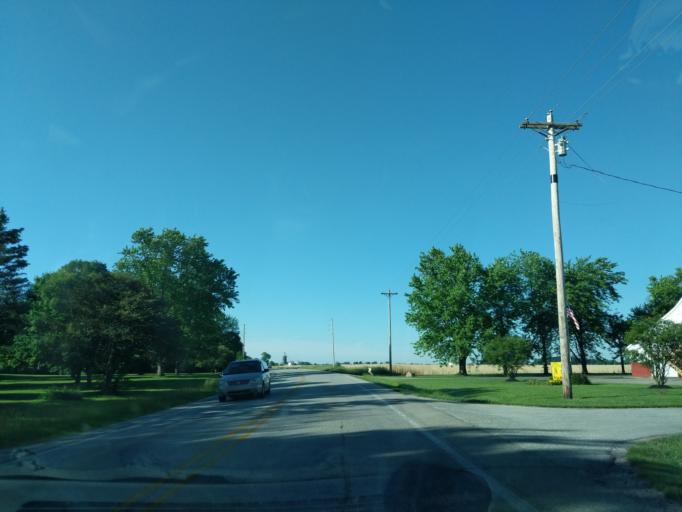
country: US
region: Indiana
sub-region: Shelby County
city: Shelbyville
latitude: 39.5961
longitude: -85.7766
